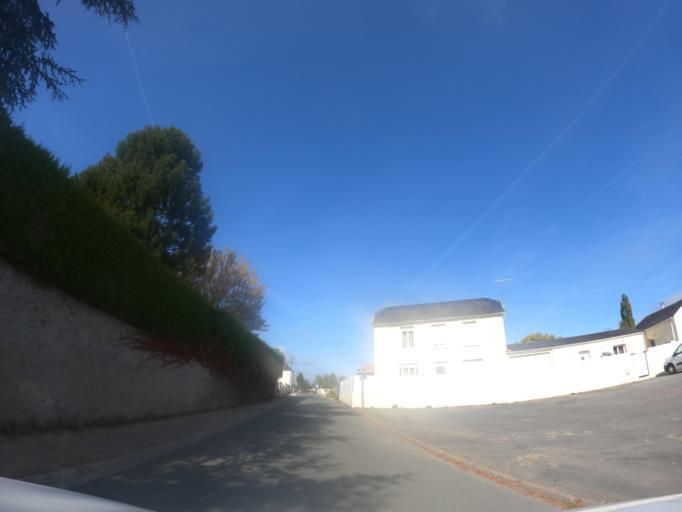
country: FR
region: Poitou-Charentes
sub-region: Departement des Deux-Sevres
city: Courlay
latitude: 46.7804
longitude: -0.5667
